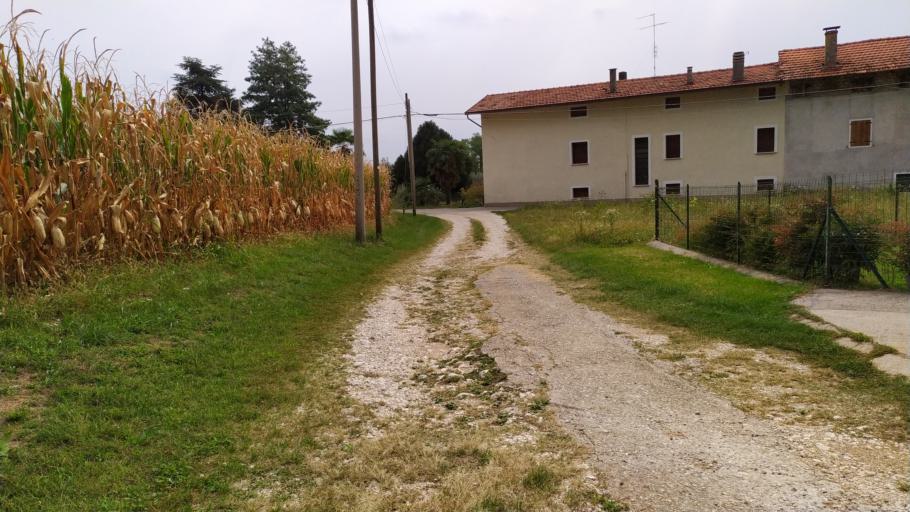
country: IT
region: Friuli Venezia Giulia
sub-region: Provincia di Pordenone
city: Aviano-Castello
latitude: 46.0808
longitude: 12.5759
